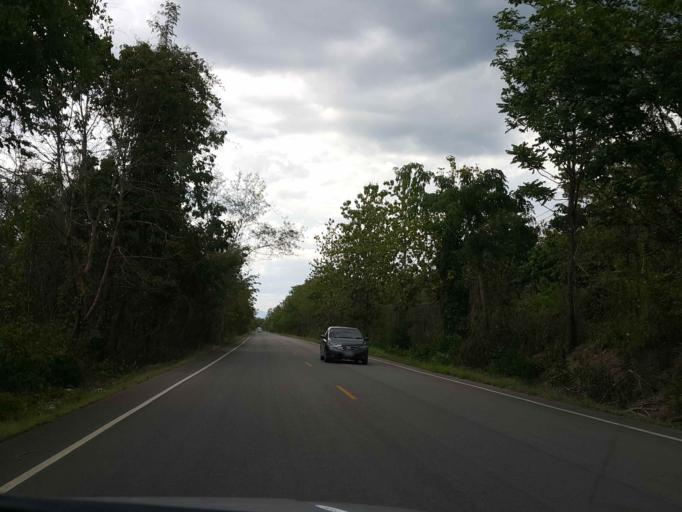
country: TH
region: Sukhothai
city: Thung Saliam
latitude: 17.3695
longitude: 99.4062
